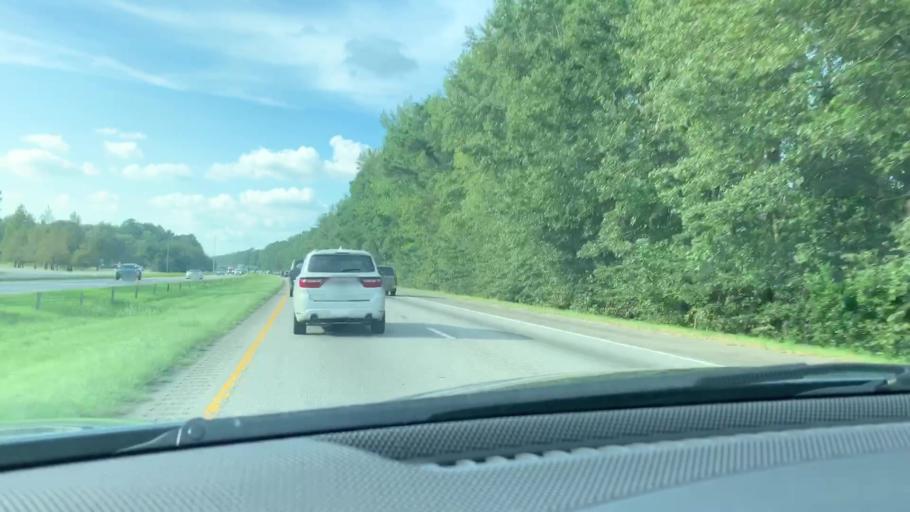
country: US
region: South Carolina
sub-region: Orangeburg County
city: Brookdale
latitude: 33.4989
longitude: -80.7686
